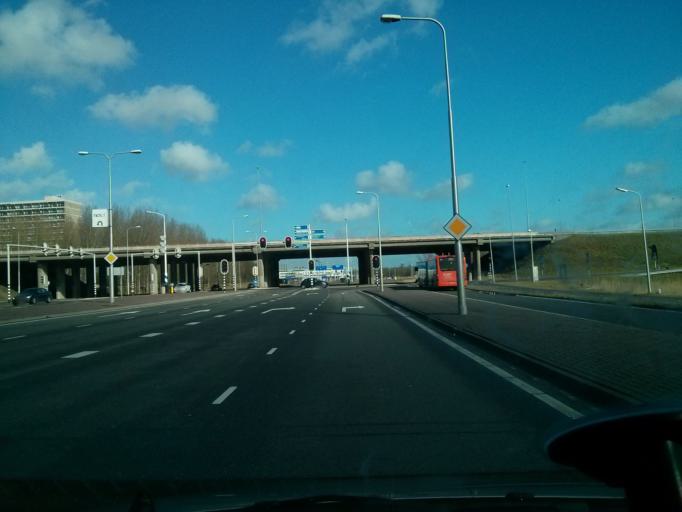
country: NL
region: North Holland
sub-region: Gemeente Amstelveen
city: Amstelveen
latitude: 52.2953
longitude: 4.8784
